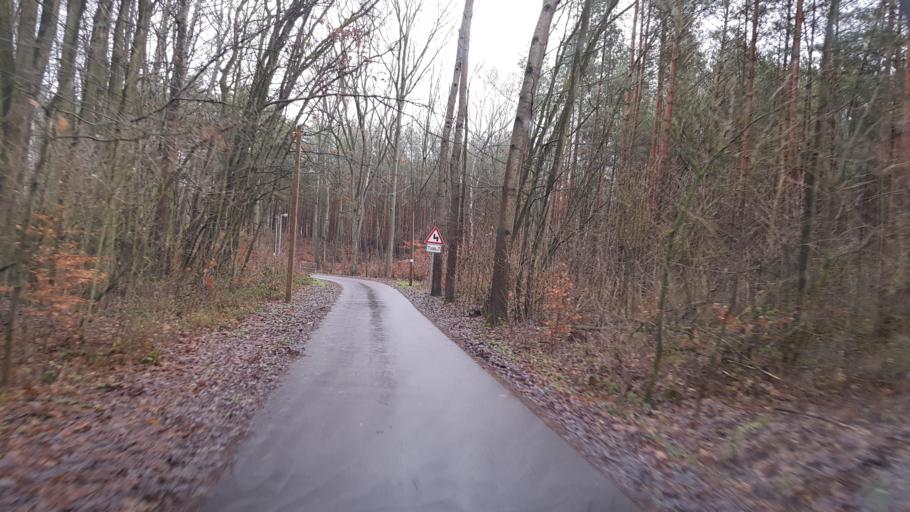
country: DE
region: Brandenburg
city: Altdobern
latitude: 51.6861
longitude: 14.0026
